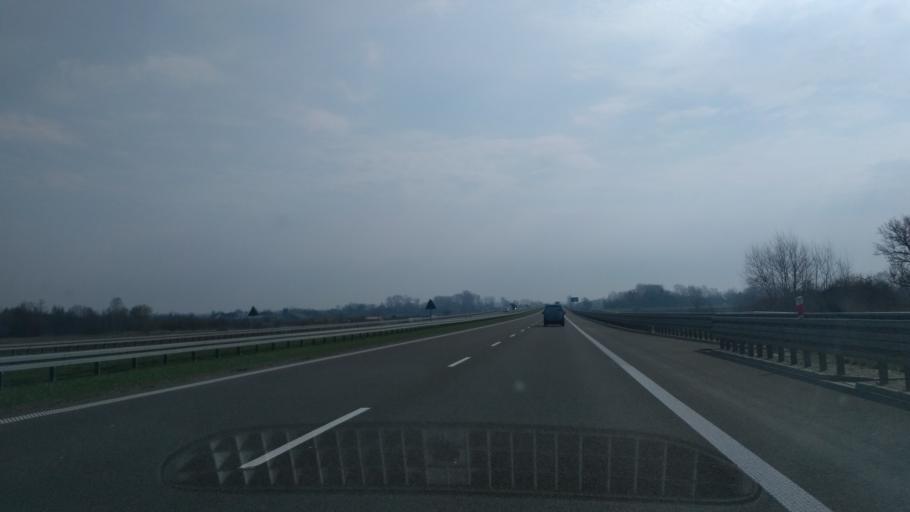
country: PL
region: Subcarpathian Voivodeship
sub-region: Powiat lancucki
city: Gluchow
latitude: 50.1001
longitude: 22.2611
